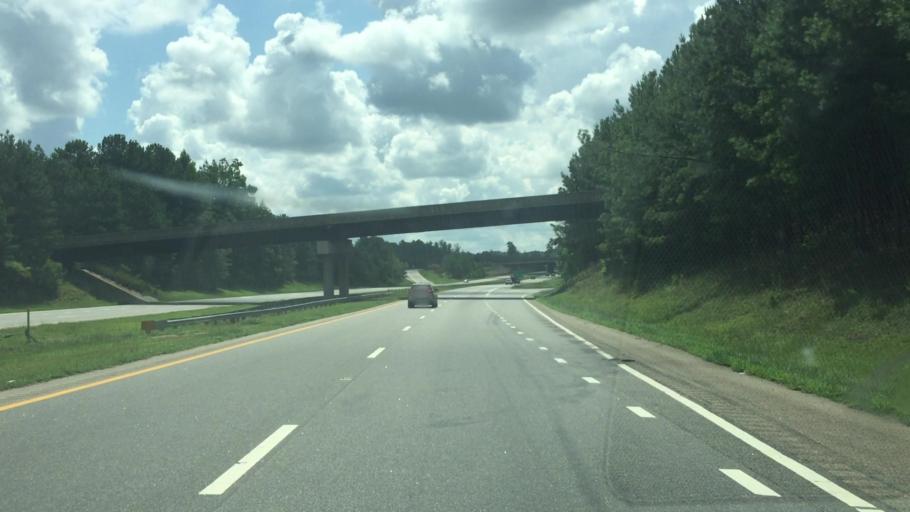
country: US
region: North Carolina
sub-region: Richmond County
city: Cordova
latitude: 34.9147
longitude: -79.7966
